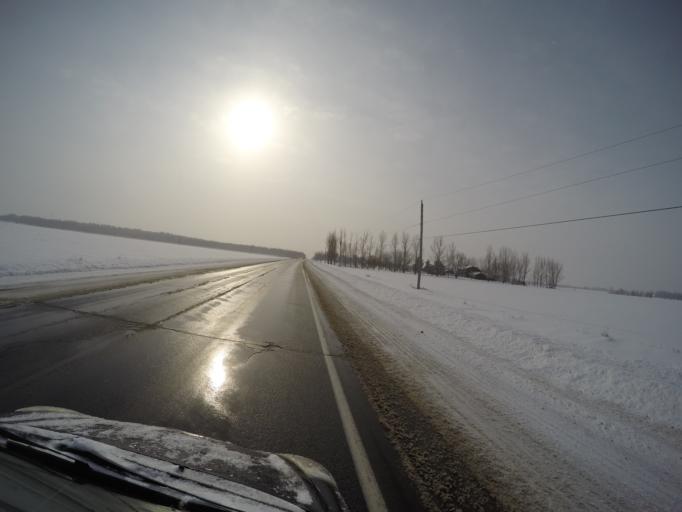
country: CA
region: Ontario
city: Clarence-Rockland
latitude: 45.4419
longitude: -75.4190
